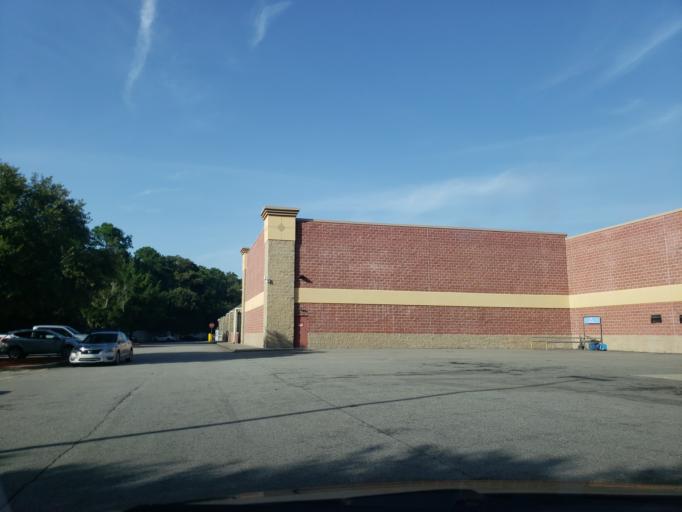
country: US
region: Georgia
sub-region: Chatham County
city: Isle of Hope
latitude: 31.9869
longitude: -81.0838
